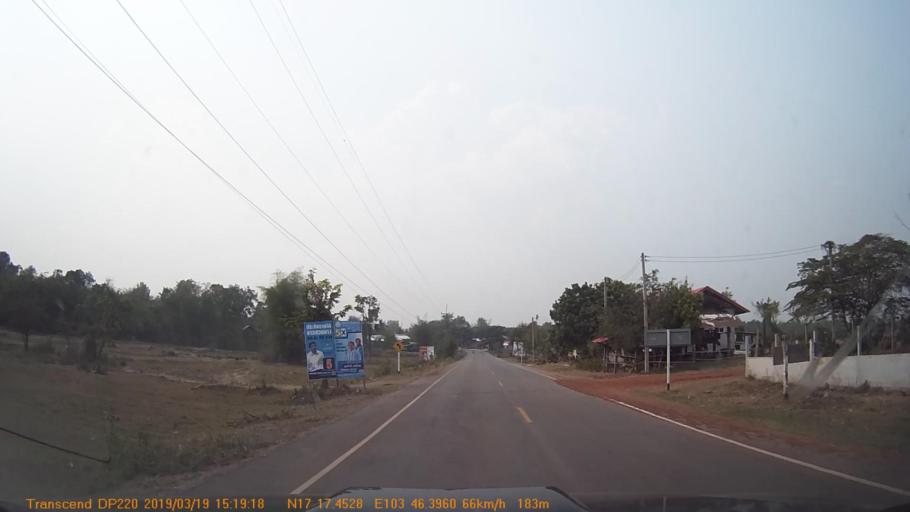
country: TH
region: Sakon Nakhon
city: Phanna Nikhom
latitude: 17.2911
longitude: 103.7731
